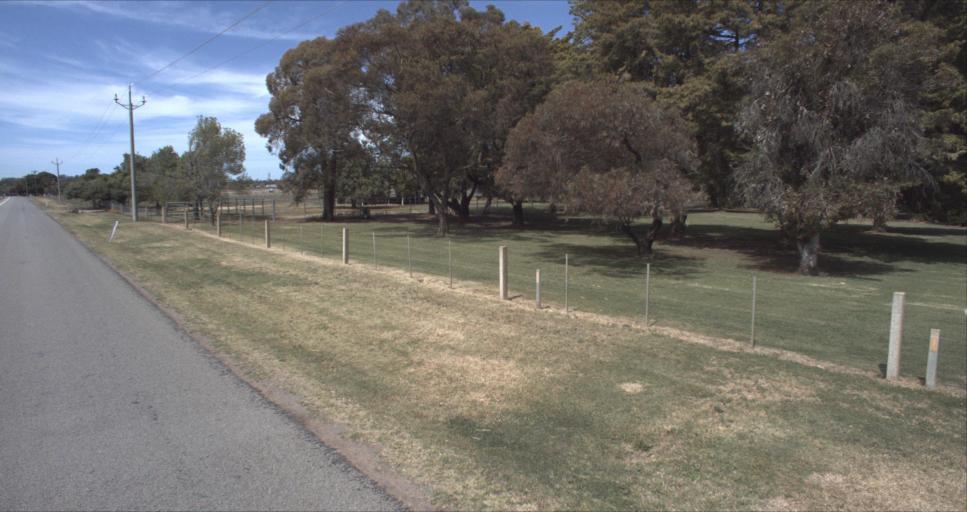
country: AU
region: New South Wales
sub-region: Leeton
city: Leeton
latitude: -34.5570
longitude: 146.4401
